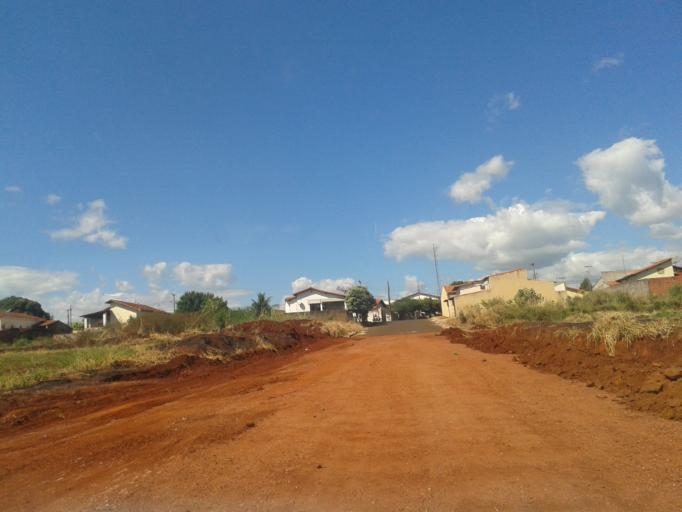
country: BR
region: Minas Gerais
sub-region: Capinopolis
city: Capinopolis
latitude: -18.6911
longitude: -49.5700
